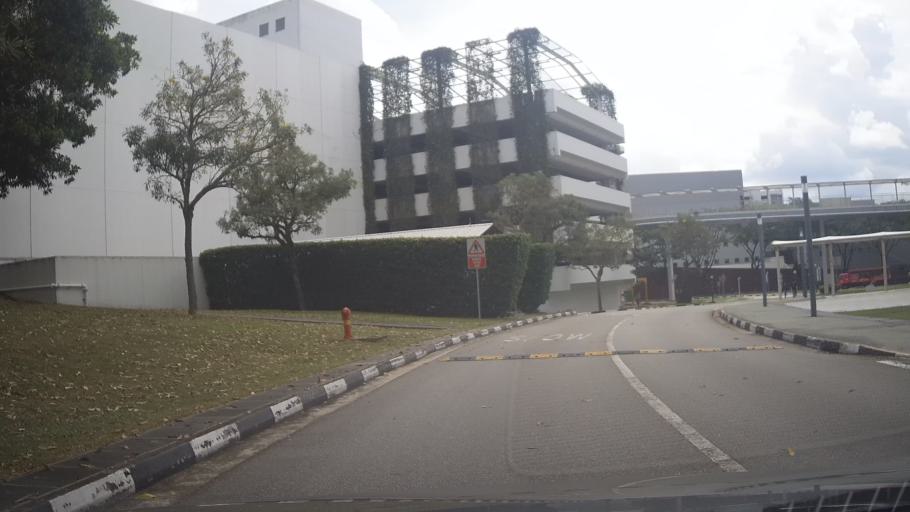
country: MY
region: Johor
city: Johor Bahru
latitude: 1.4454
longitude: 103.7860
